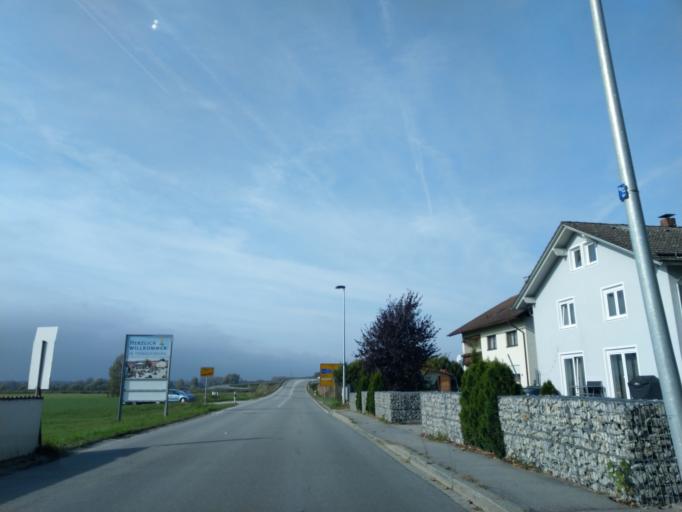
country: DE
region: Bavaria
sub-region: Lower Bavaria
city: Hengersberg
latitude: 48.7812
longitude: 13.0486
